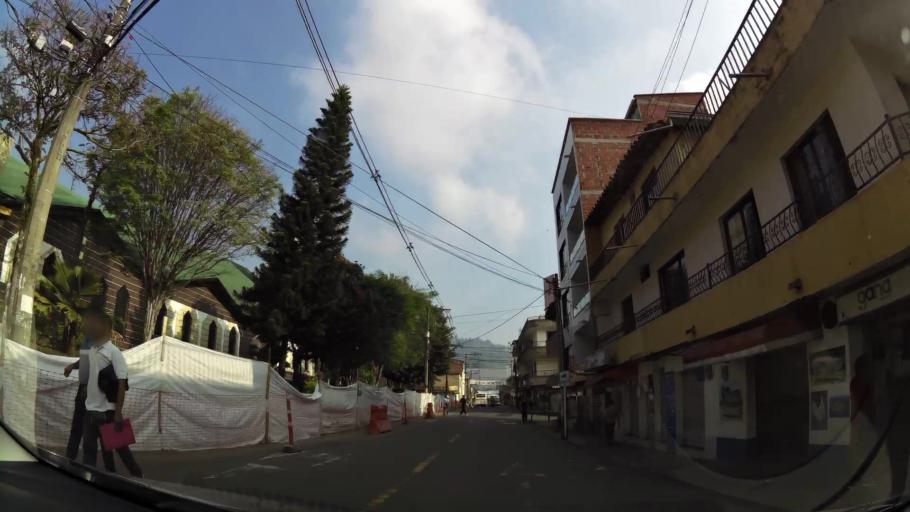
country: CO
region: Antioquia
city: Sabaneta
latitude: 6.1642
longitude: -75.6197
